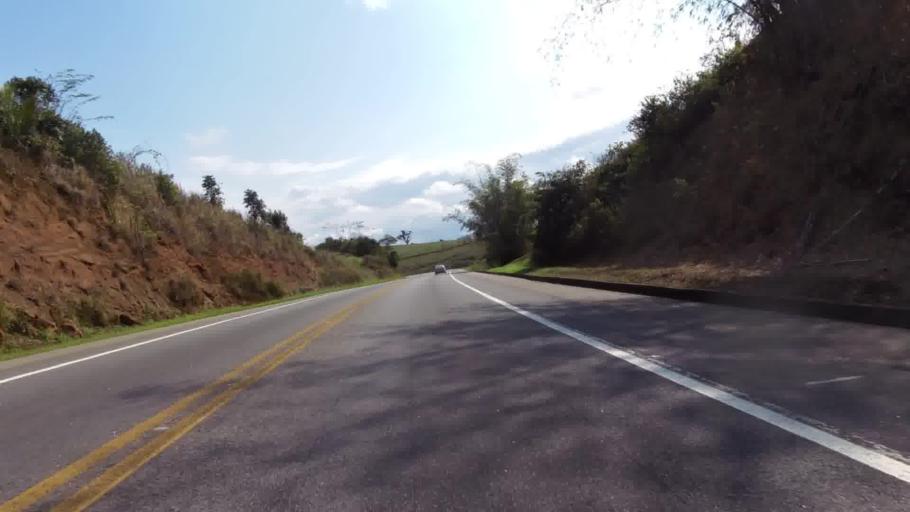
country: BR
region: Rio de Janeiro
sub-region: Macae
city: Macae
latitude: -22.2492
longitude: -41.8134
